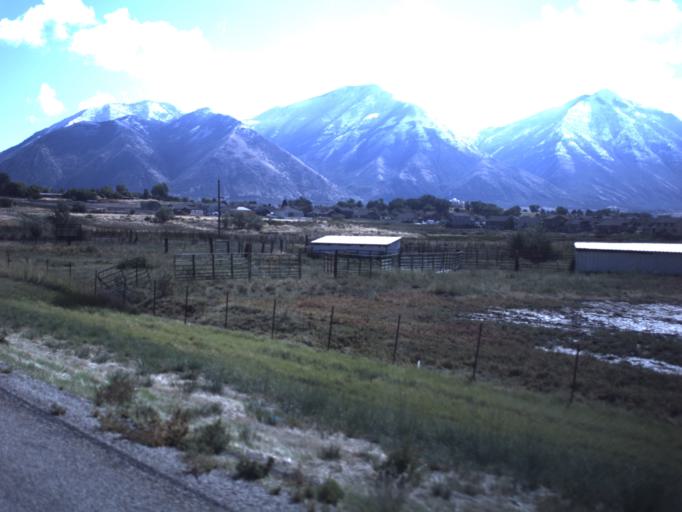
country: US
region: Utah
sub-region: Utah County
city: Salem
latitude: 40.0852
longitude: -111.6739
